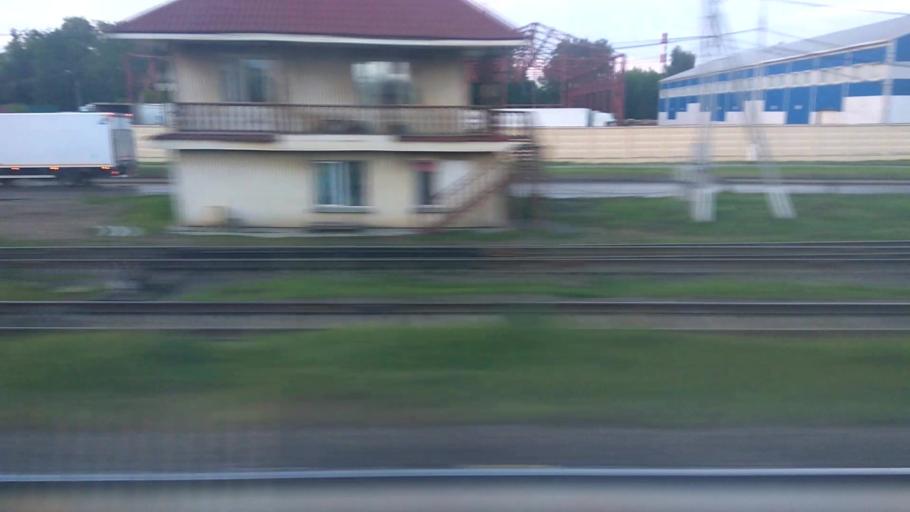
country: RU
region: Moskovskaya
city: Domodedovo
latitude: 55.4482
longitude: 37.7671
